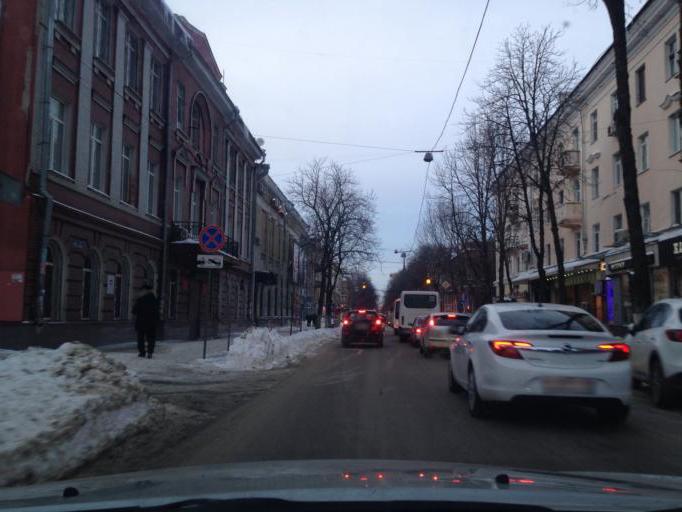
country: RU
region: Voronezj
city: Voronezh
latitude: 51.6698
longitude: 39.2051
